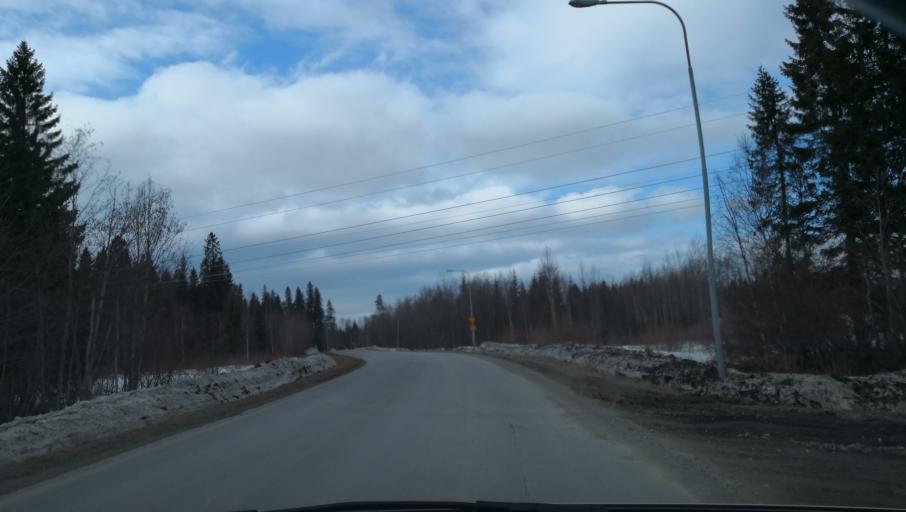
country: SE
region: Vaesterbotten
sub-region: Vannas Kommun
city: Vaennaes
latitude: 63.9175
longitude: 19.7423
